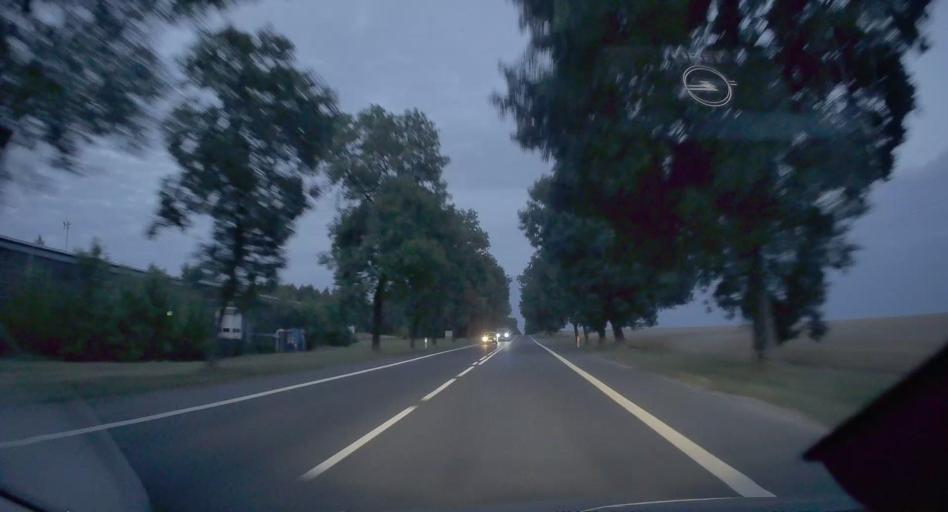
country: PL
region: Silesian Voivodeship
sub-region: Powiat klobucki
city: Klobuck
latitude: 50.9110
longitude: 18.9061
